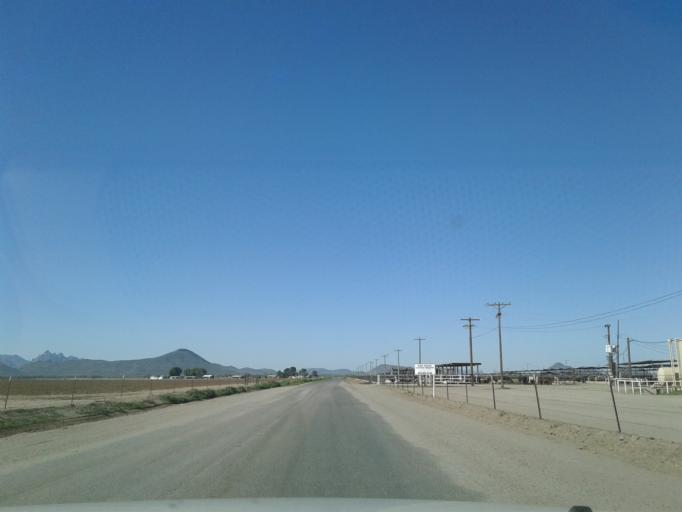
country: US
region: Arizona
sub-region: Pima County
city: Avra Valley
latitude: 32.5574
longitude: -111.3722
